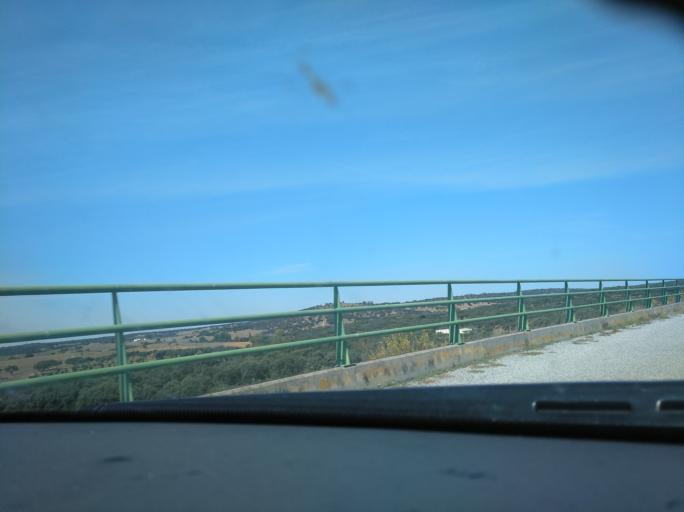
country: PT
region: Evora
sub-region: Montemor-O-Novo
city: Montemor-o-Novo
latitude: 38.6559
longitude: -8.0983
